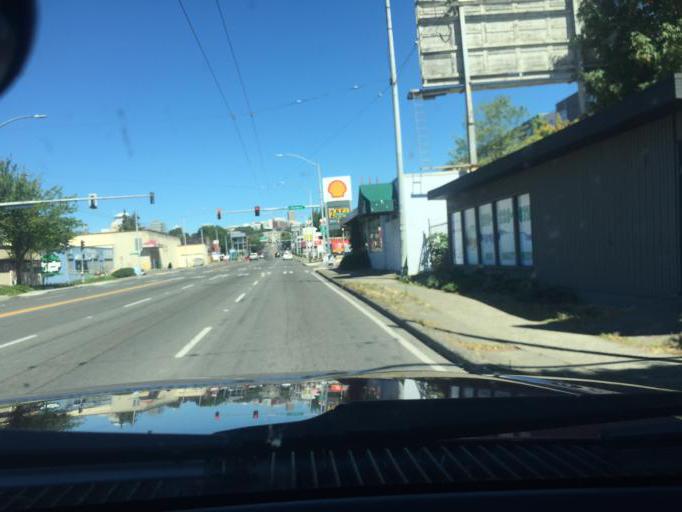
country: US
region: Washington
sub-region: King County
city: Seattle
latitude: 47.5936
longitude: -122.3097
